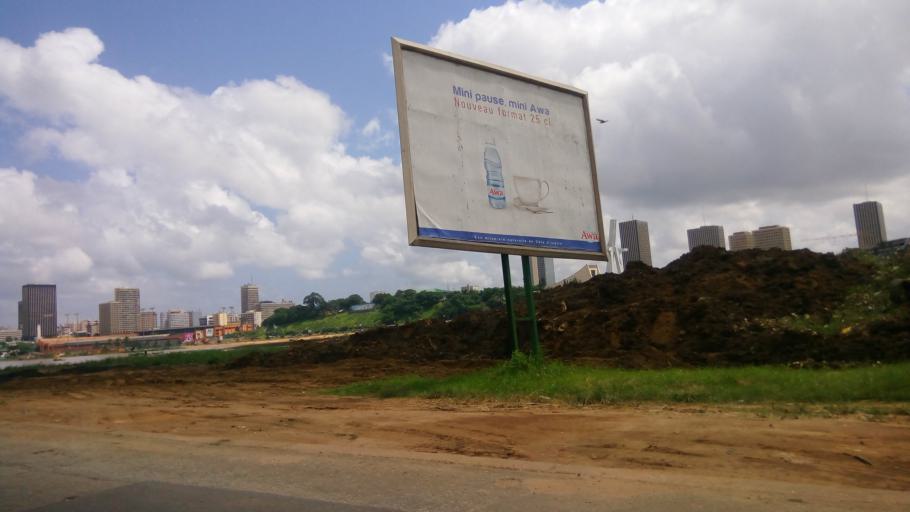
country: CI
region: Lagunes
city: Abidjan
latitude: 5.3365
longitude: -4.0142
